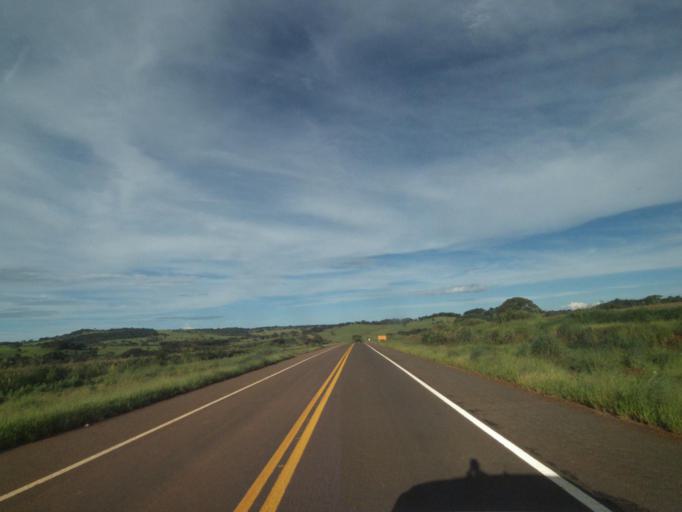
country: BR
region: Goias
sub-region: Jaragua
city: Jaragua
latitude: -15.9009
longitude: -49.5314
